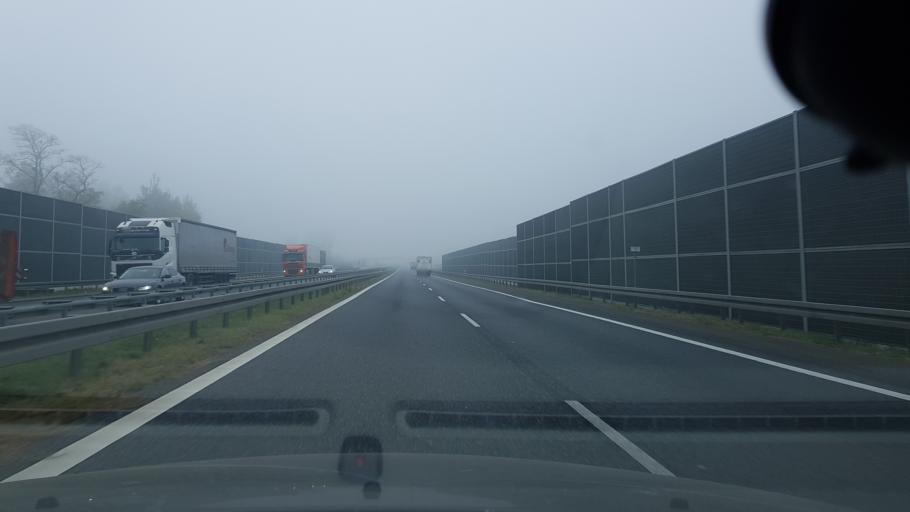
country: PL
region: Masovian Voivodeship
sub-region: Powiat zyrardowski
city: Mszczonow
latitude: 51.9569
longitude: 20.4959
